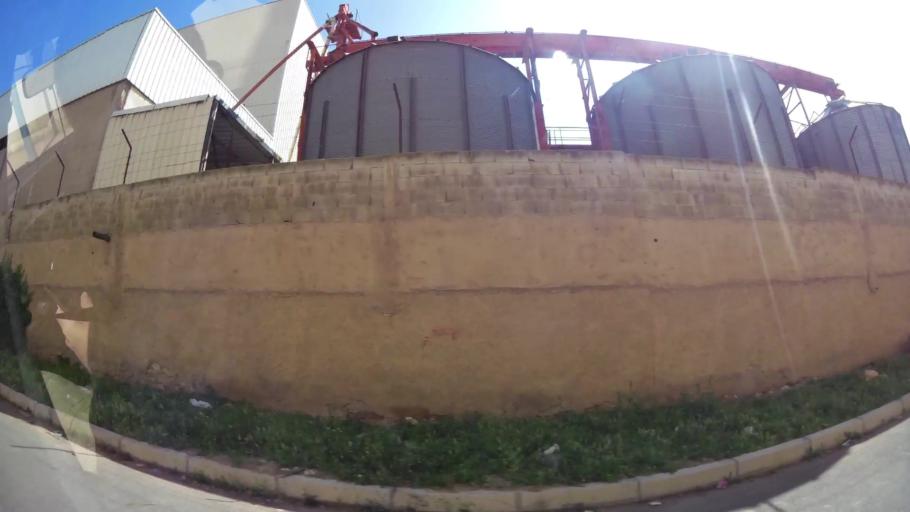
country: MA
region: Oriental
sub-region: Oujda-Angad
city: Oujda
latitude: 34.6963
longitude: -1.8778
